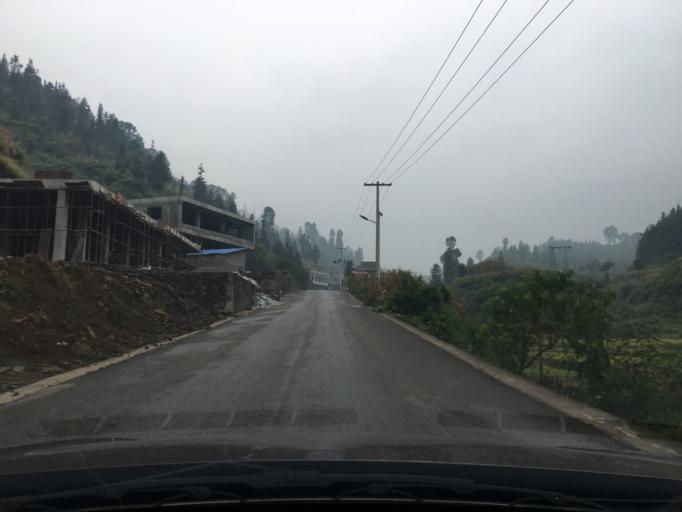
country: CN
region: Guizhou Sheng
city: Liupanshui
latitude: 26.0582
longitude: 105.1304
